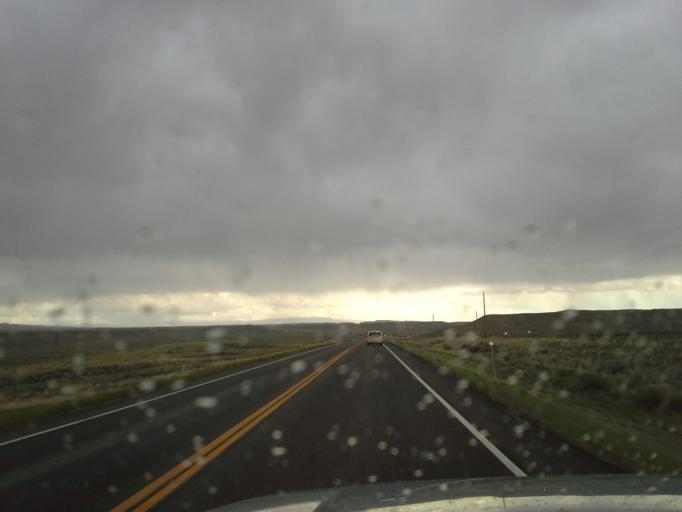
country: US
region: Wyoming
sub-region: Park County
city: Powell
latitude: 45.0697
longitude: -108.6796
